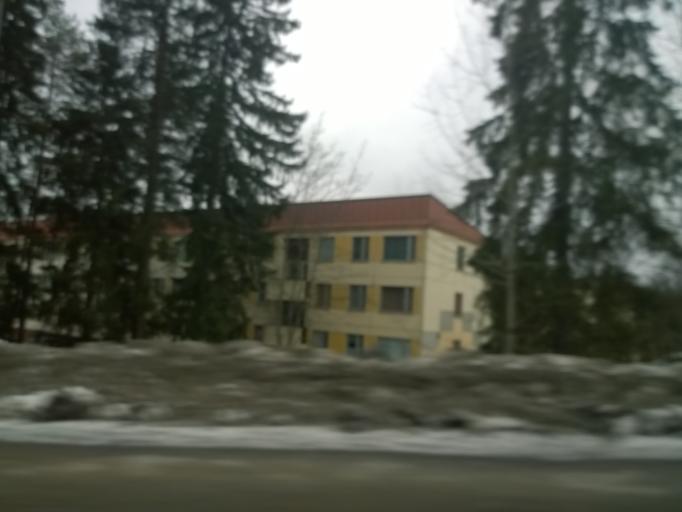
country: FI
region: Pirkanmaa
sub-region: Tampere
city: Tampere
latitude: 61.4172
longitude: 23.7571
